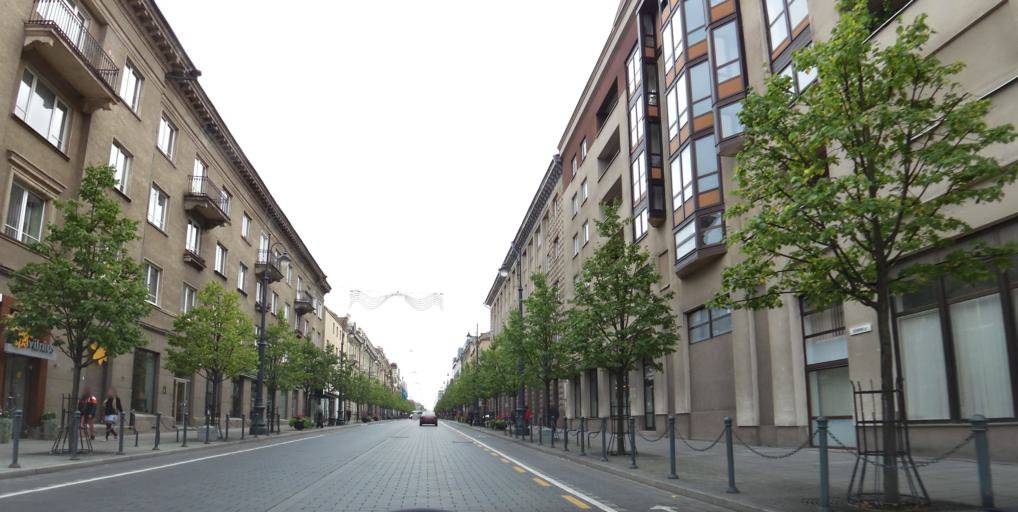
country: LT
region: Vilnius County
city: Naujamiestis
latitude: 54.6898
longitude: 25.2635
